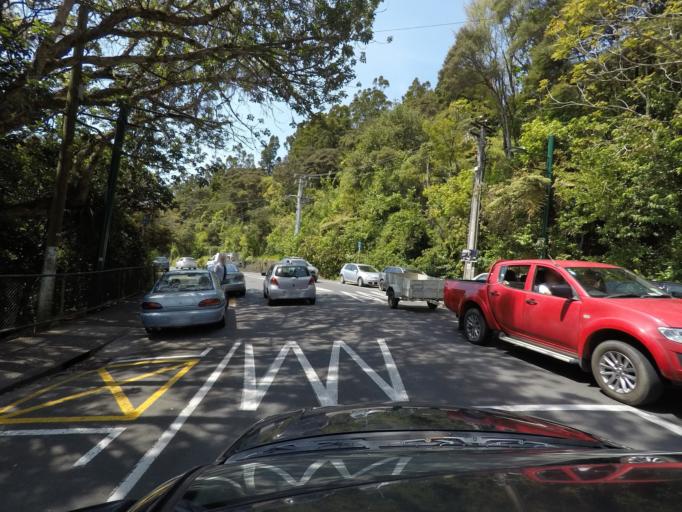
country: NZ
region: Auckland
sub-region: Auckland
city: Titirangi
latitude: -36.9376
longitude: 174.6578
